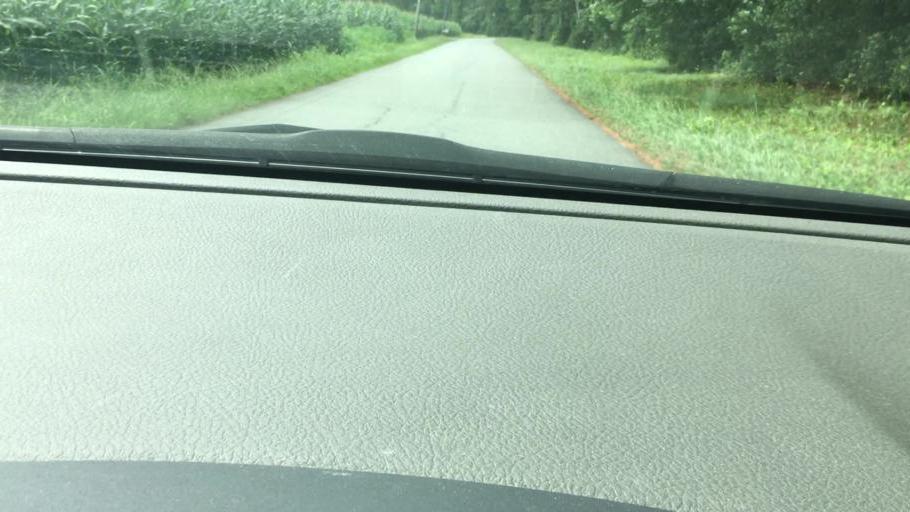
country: US
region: Maryland
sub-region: Worcester County
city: Pocomoke City
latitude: 38.0657
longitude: -75.5063
